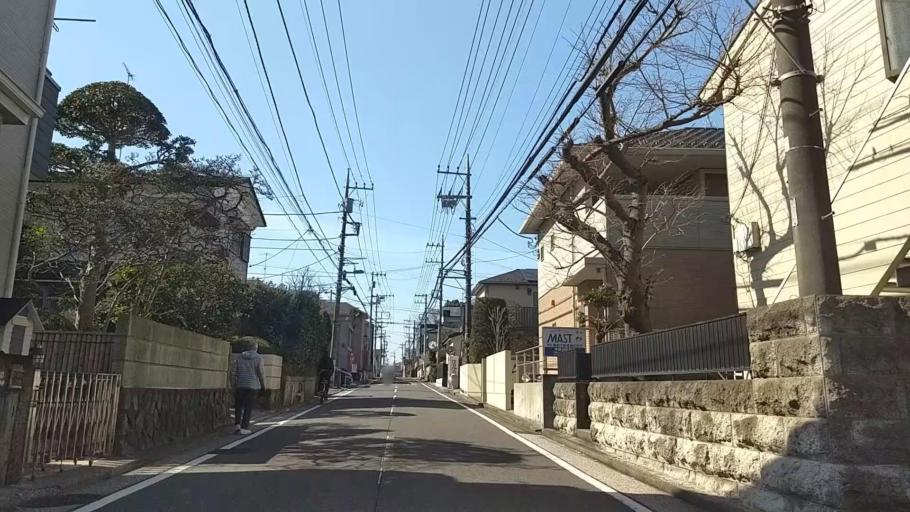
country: JP
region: Kanagawa
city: Kamakura
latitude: 35.3595
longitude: 139.5399
